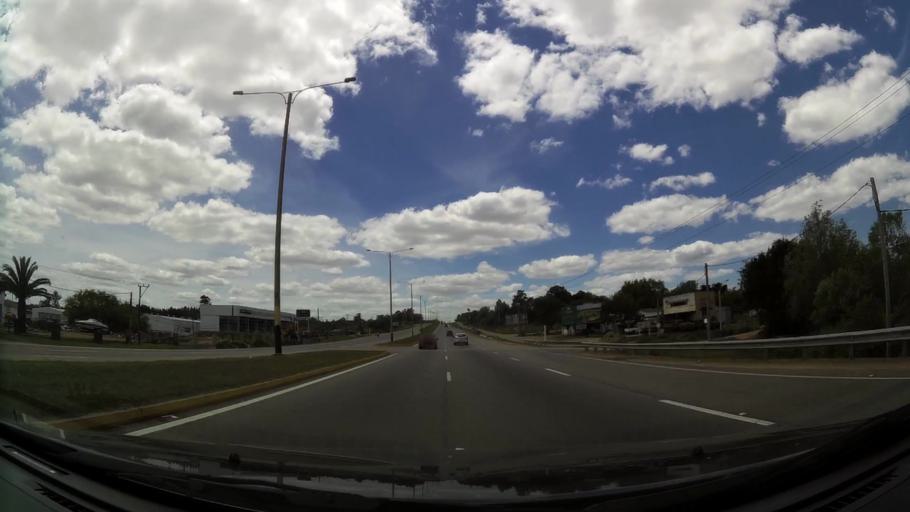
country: UY
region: Canelones
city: Colonia Nicolich
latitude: -34.8249
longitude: -55.9968
